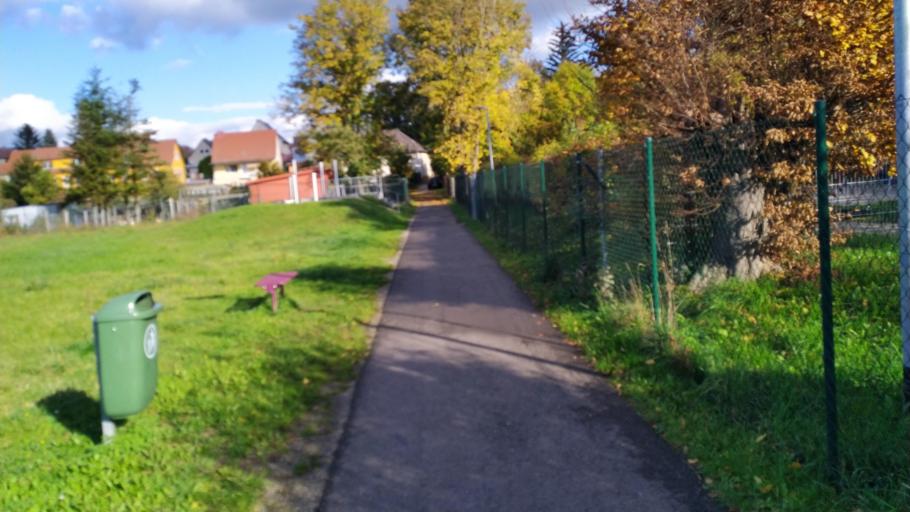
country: DE
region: Thuringia
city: Mattstedt
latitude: 51.0539
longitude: 11.5008
